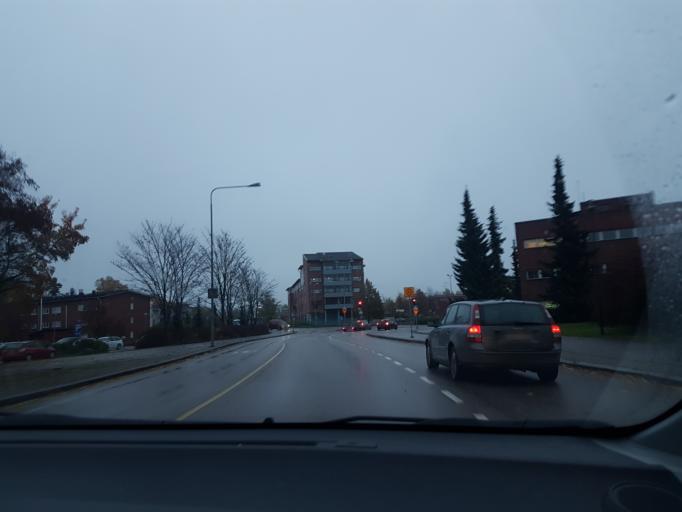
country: FI
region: Uusimaa
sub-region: Helsinki
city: Tuusula
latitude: 60.4033
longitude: 25.0241
